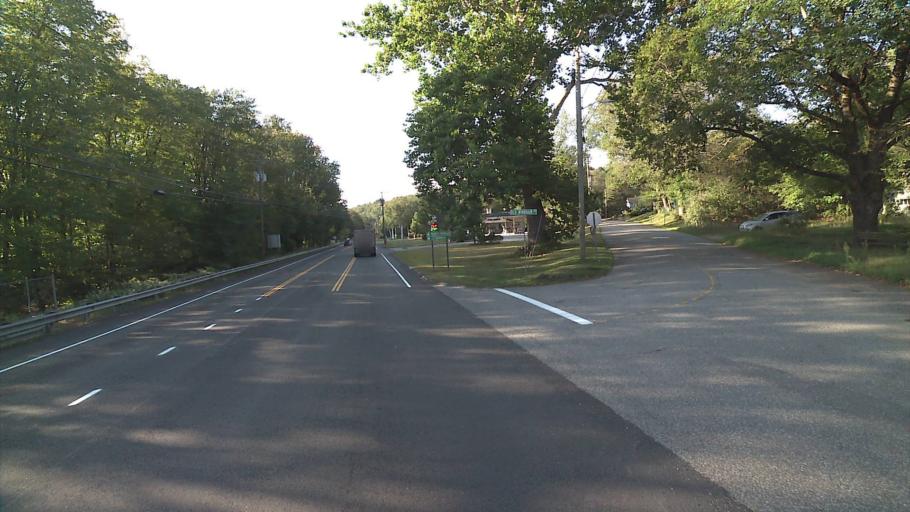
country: US
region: Connecticut
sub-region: Windham County
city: South Windham
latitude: 41.6787
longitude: -72.1686
